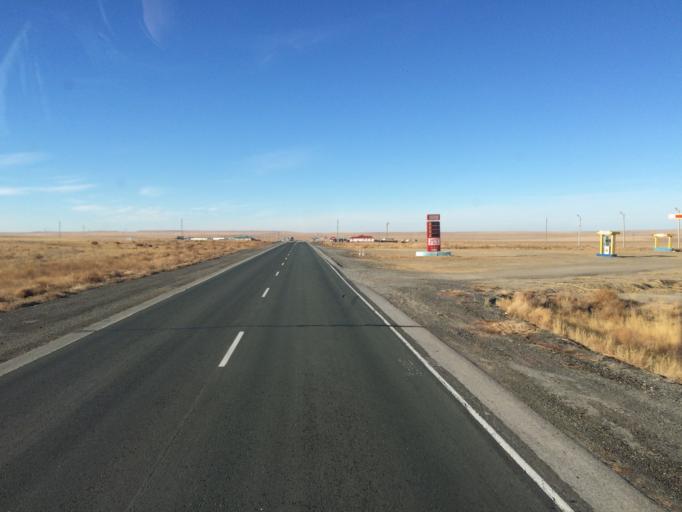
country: KZ
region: Aqtoebe
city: Yrghyz
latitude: 48.5072
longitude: 61.0121
